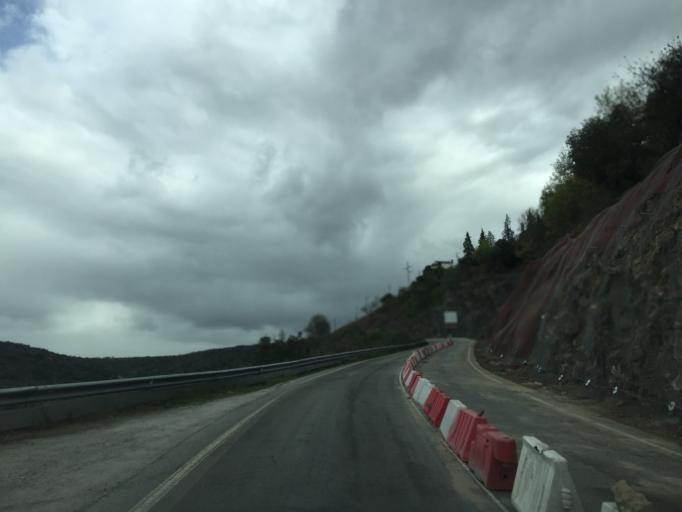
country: PT
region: Braganca
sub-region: Miranda do Douro
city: Miranda do Douro
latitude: 41.4931
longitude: -6.2701
